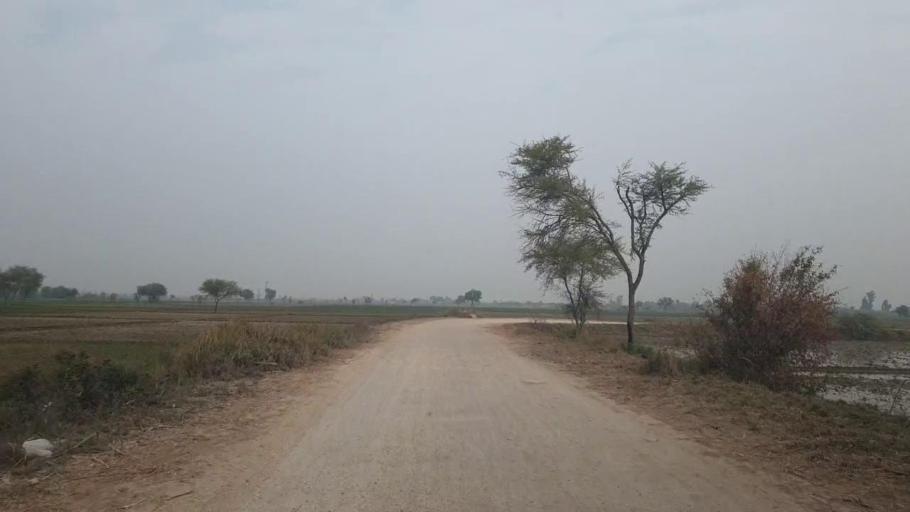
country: PK
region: Sindh
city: Tando Adam
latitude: 25.7265
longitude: 68.7145
